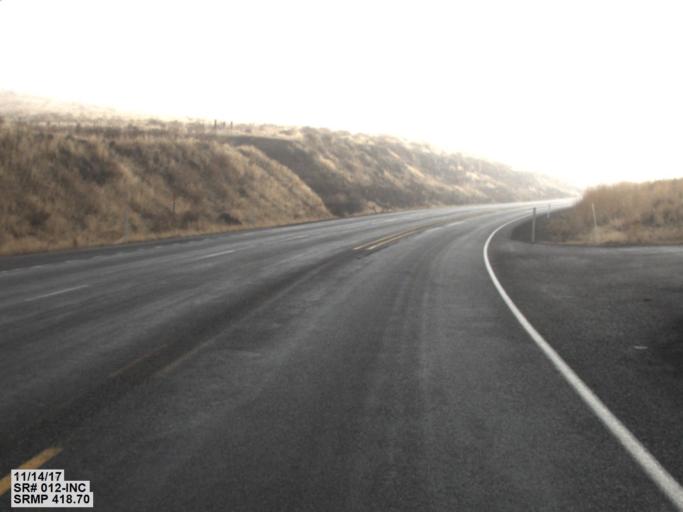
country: US
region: Washington
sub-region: Asotin County
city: Clarkston Heights-Vineland
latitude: 46.4365
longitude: -117.3238
